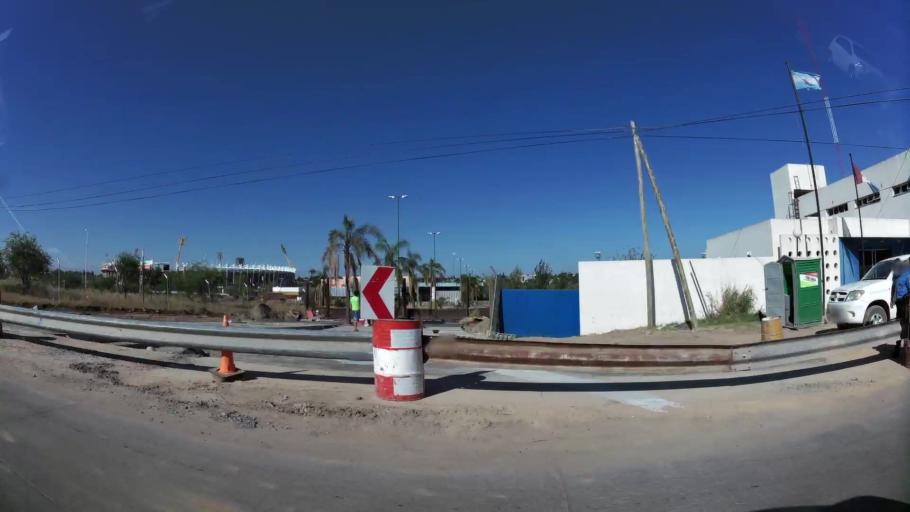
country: AR
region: Cordoba
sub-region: Departamento de Capital
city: Cordoba
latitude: -31.3724
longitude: -64.2502
